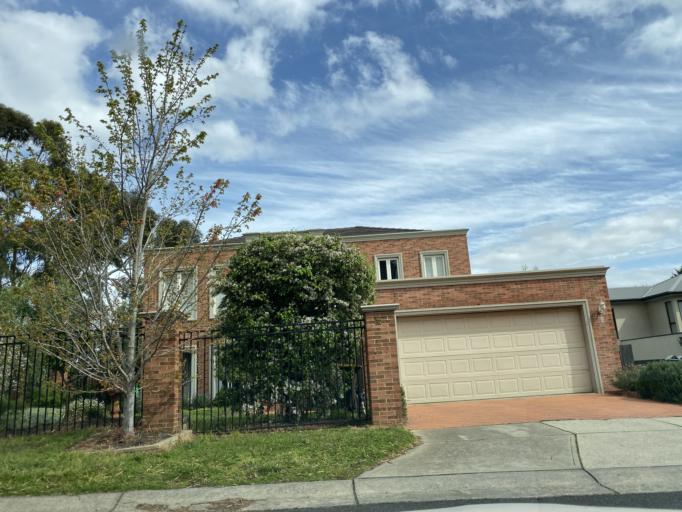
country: AU
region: Victoria
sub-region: Whitehorse
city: Surrey Hills
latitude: -37.8436
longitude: 145.1015
